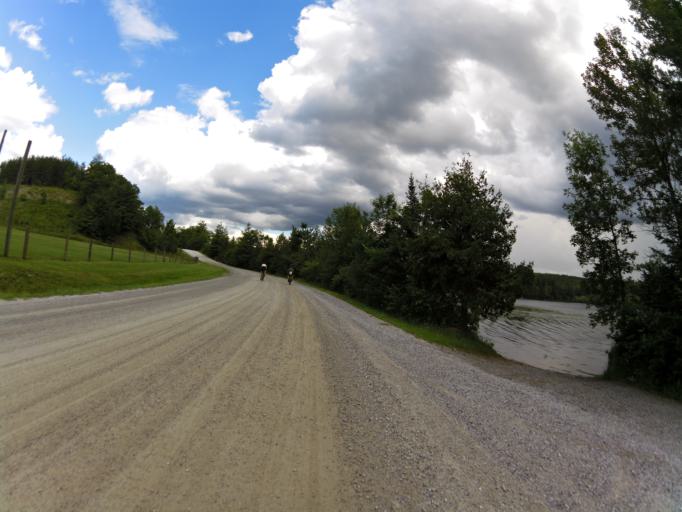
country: CA
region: Ontario
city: Renfrew
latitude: 45.1346
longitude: -76.6359
